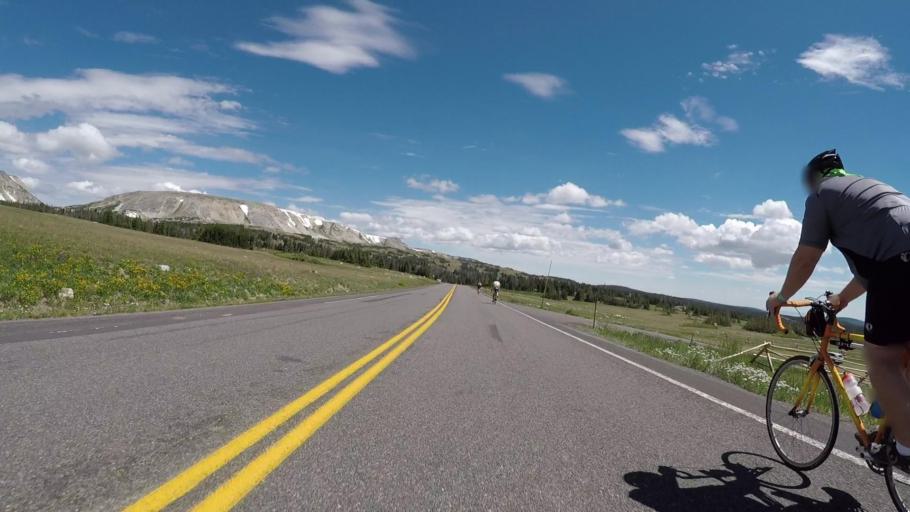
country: US
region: Wyoming
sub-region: Carbon County
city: Saratoga
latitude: 41.3455
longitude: -106.2919
